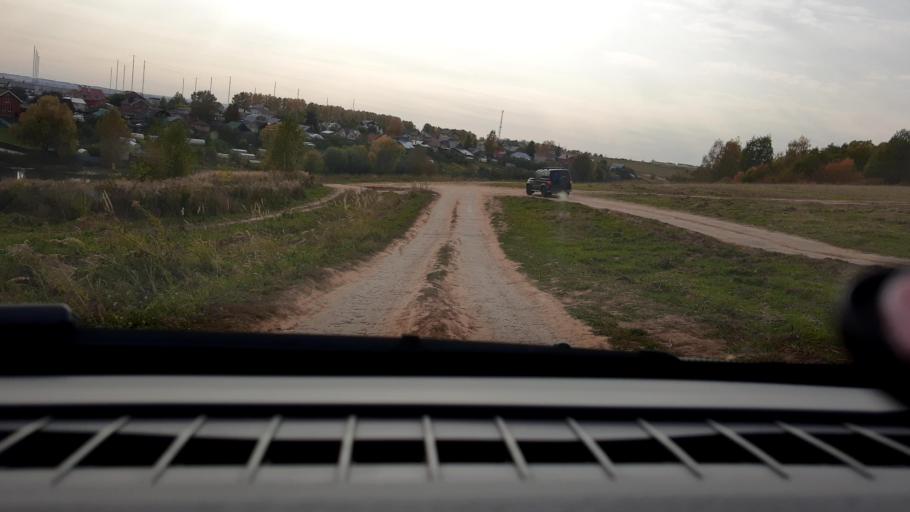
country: RU
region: Nizjnij Novgorod
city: Nizhniy Novgorod
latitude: 56.2000
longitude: 43.9634
